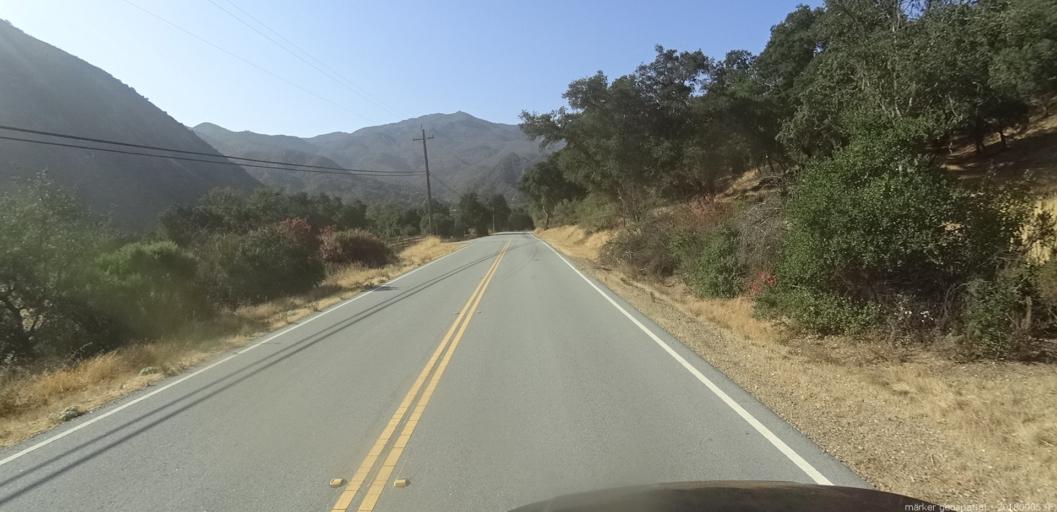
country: US
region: California
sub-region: Monterey County
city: Greenfield
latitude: 36.2448
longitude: -121.4324
